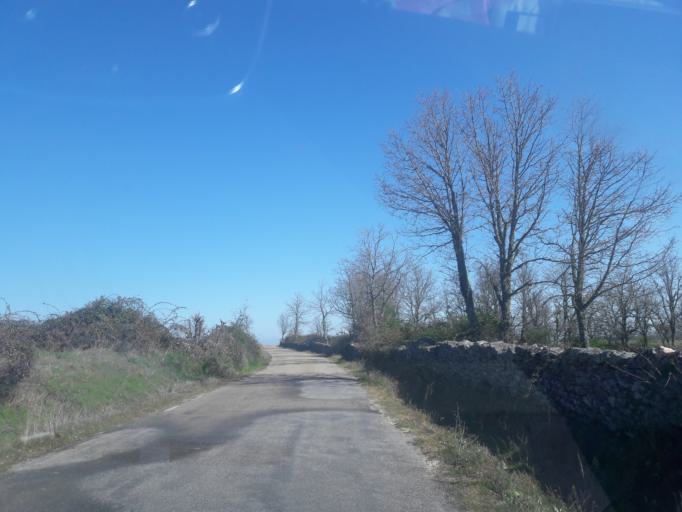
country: ES
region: Castille and Leon
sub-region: Provincia de Salamanca
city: Valsalabroso
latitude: 41.1326
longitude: -6.4825
